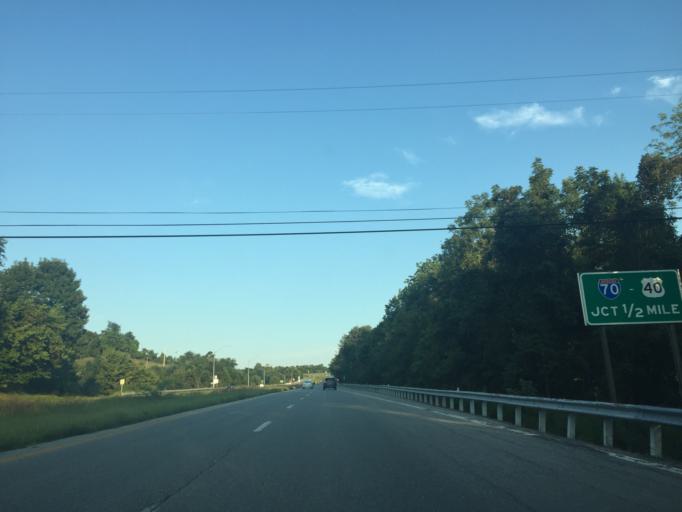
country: US
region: Maryland
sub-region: Frederick County
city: Spring Ridge
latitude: 39.3939
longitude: -77.3325
